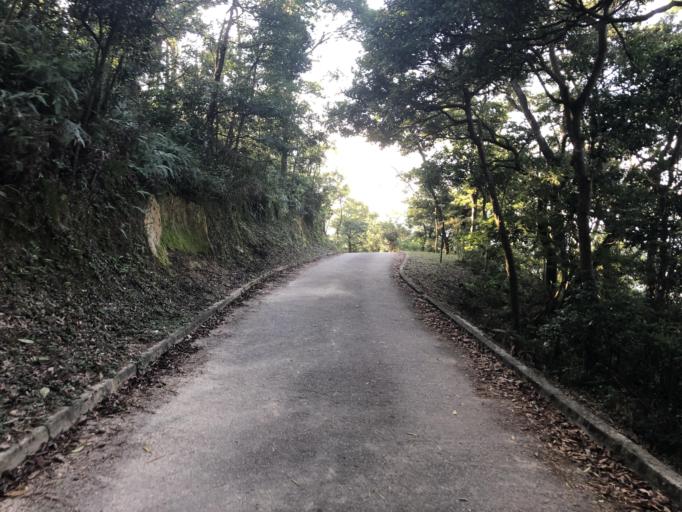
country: HK
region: Tsuen Wan
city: Tsuen Wan
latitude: 22.3971
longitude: 114.0790
